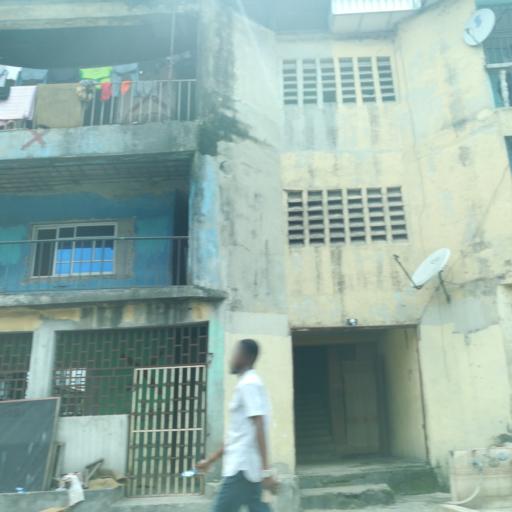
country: NG
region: Rivers
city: Port Harcourt
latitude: 4.8071
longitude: 7.0025
